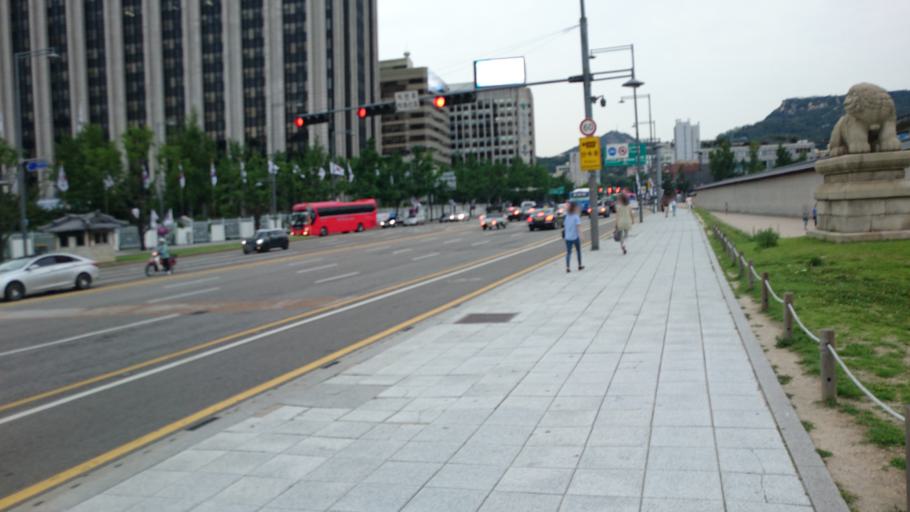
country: KR
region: Seoul
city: Seoul
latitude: 37.5758
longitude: 126.9766
